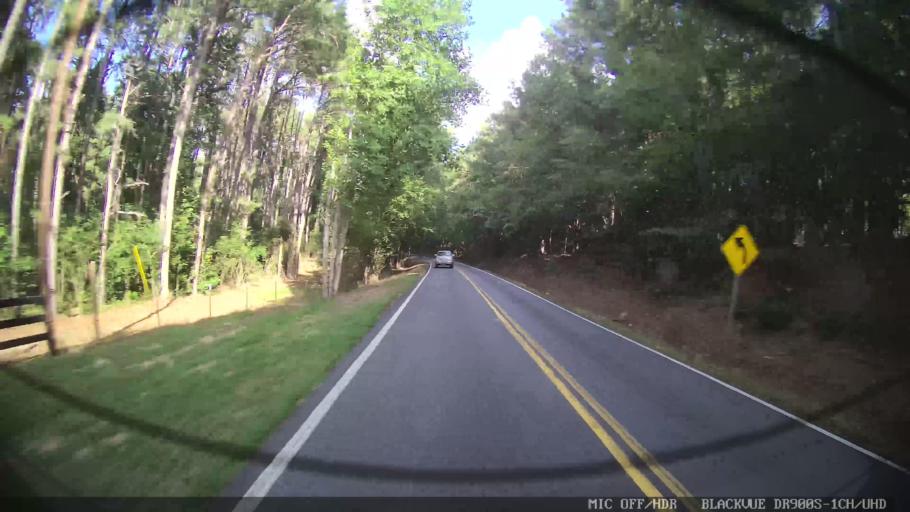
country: US
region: Georgia
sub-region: Floyd County
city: Lindale
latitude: 34.1948
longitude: -85.0745
